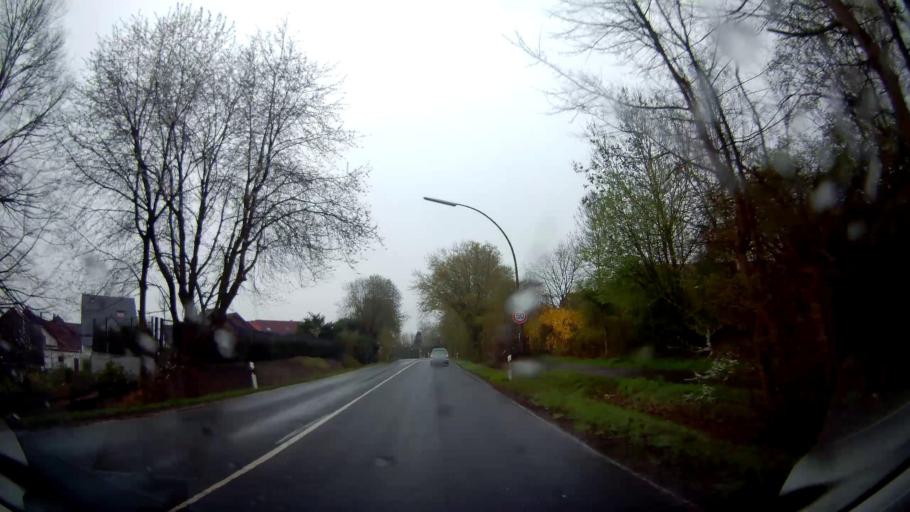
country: DE
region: North Rhine-Westphalia
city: Castrop-Rauxel
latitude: 51.5333
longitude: 7.3444
